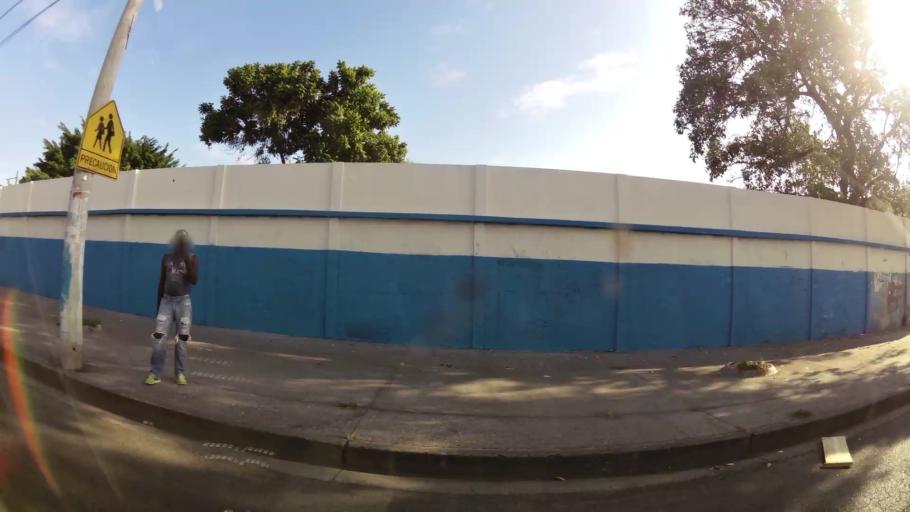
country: EC
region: Guayas
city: Guayaquil
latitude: -2.2183
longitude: -79.9187
